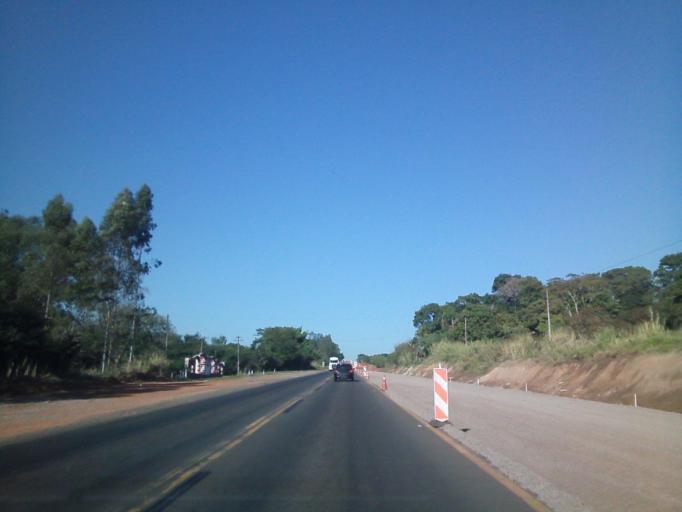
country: BR
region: Sao Paulo
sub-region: Pirapozinho
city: Pirapozinho
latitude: -22.2191
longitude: -51.4390
